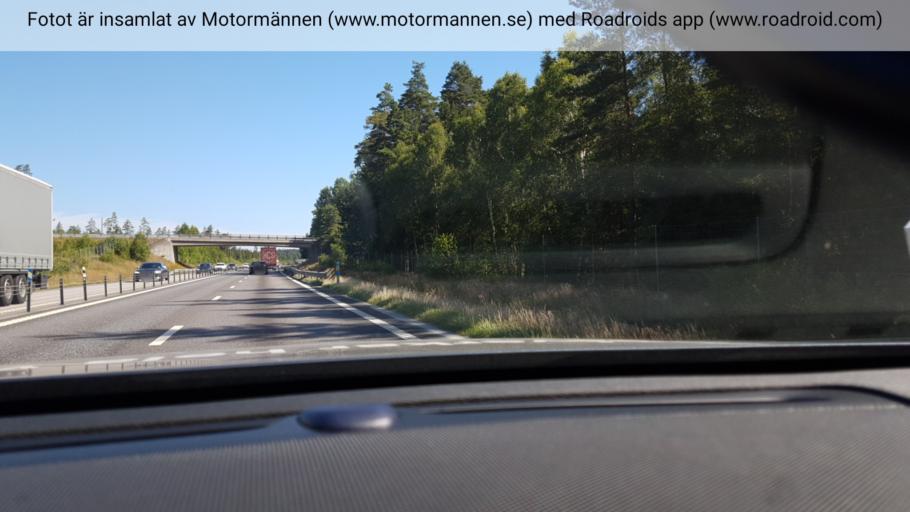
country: SE
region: Kronoberg
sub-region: Ljungby Kommun
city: Ljungby
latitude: 56.7800
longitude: 13.8825
